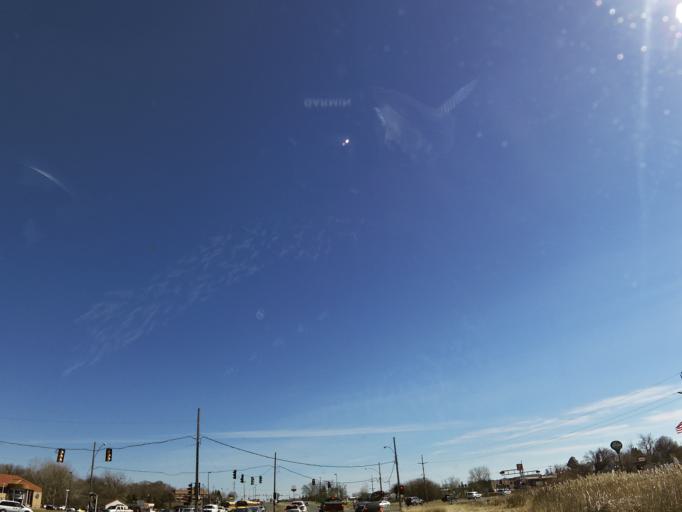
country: US
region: Minnesota
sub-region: Wright County
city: Buffalo
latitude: 45.1826
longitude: -93.8770
